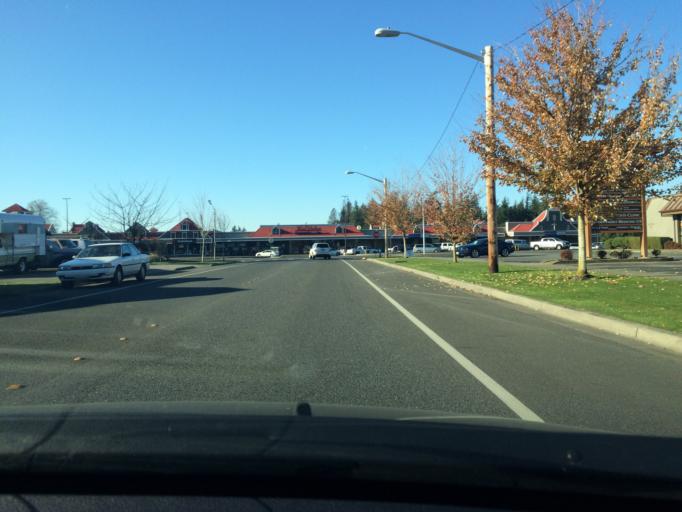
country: US
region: Washington
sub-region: Whatcom County
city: Lynden
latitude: 48.9407
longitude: -122.4680
